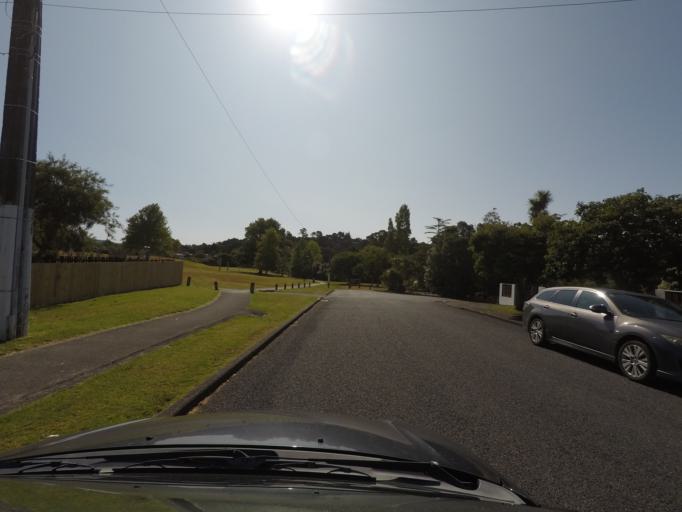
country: NZ
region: Auckland
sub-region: Auckland
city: Rosebank
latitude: -36.8558
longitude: 174.6190
